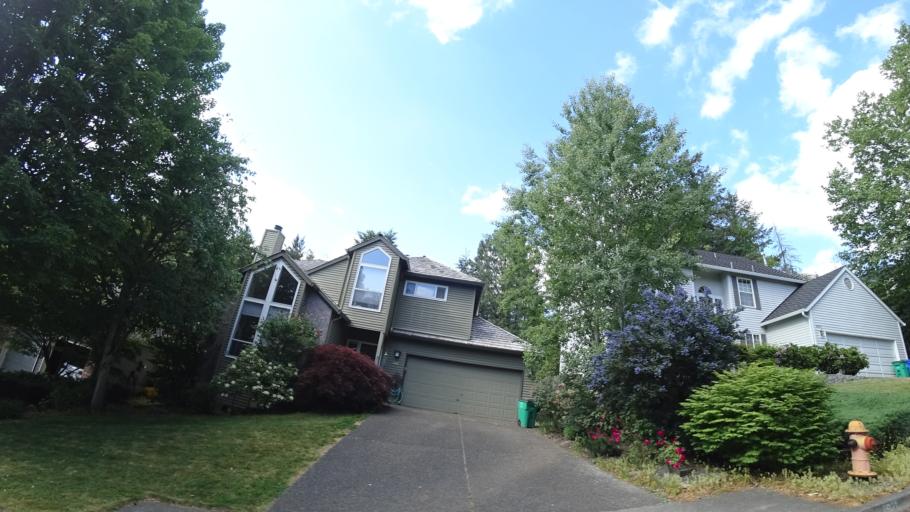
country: US
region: Oregon
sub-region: Washington County
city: Garden Home-Whitford
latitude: 45.4663
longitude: -122.7274
